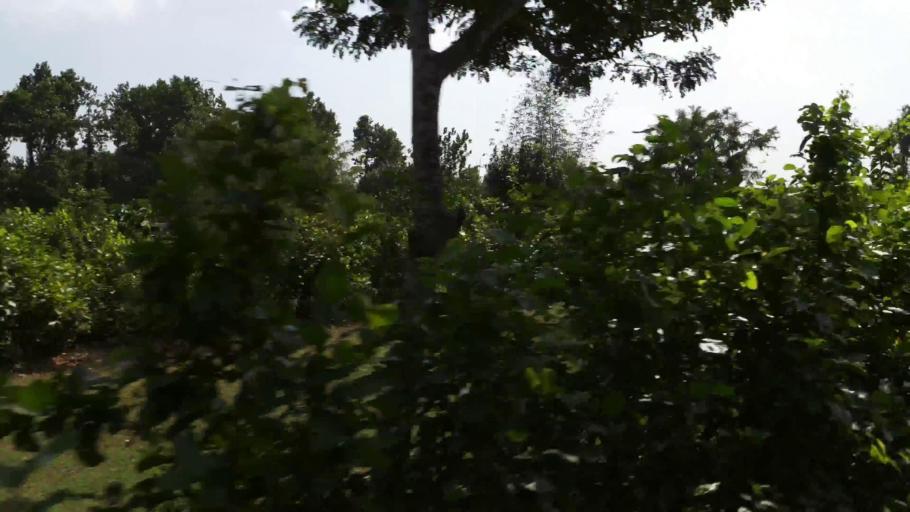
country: BD
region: Dhaka
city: Tungi
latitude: 24.1633
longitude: 90.4687
